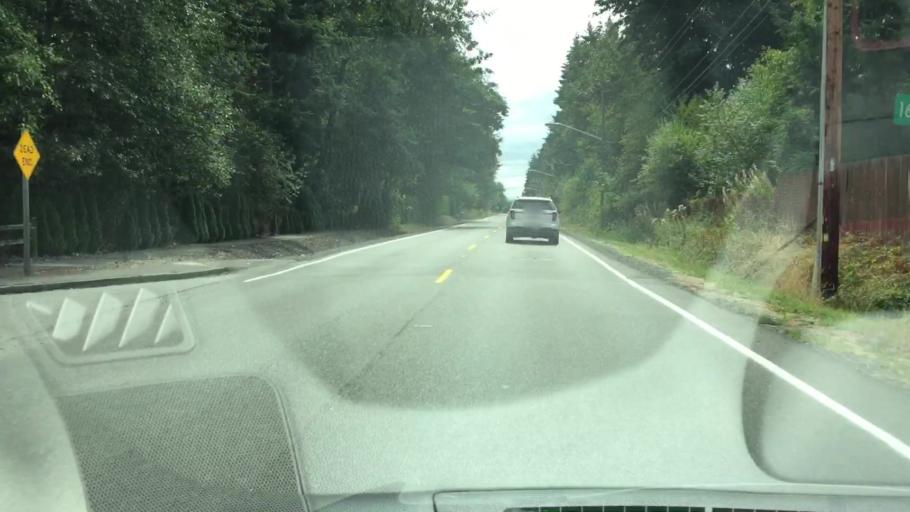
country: US
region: Washington
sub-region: Pierce County
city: South Hill
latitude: 47.1106
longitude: -122.2667
